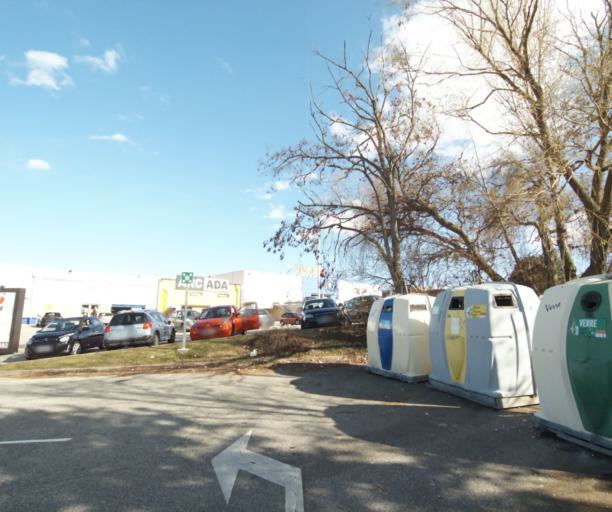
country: FR
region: Rhone-Alpes
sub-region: Departement de l'Ardeche
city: Davezieux
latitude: 45.2554
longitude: 4.6880
